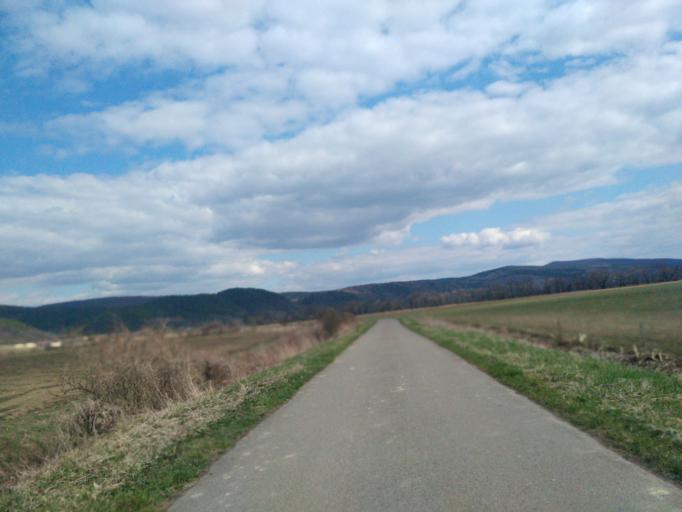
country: PL
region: Subcarpathian Voivodeship
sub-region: Powiat brzozowski
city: Dydnia
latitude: 49.6690
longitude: 22.2588
